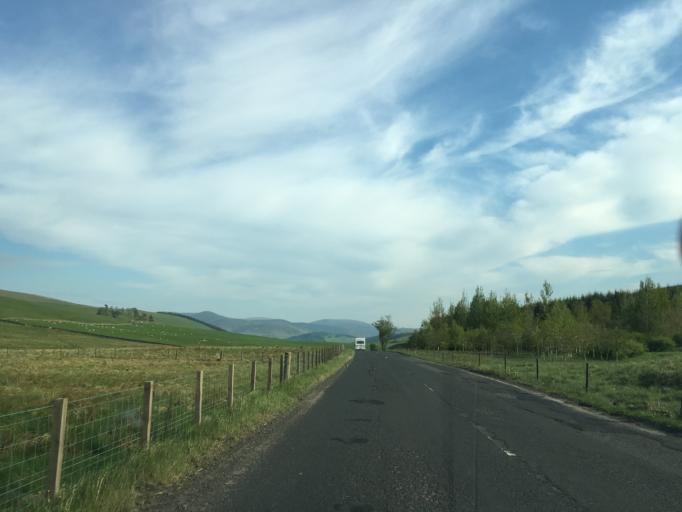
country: GB
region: Scotland
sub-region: South Lanarkshire
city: Biggar
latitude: 55.6437
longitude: -3.4273
